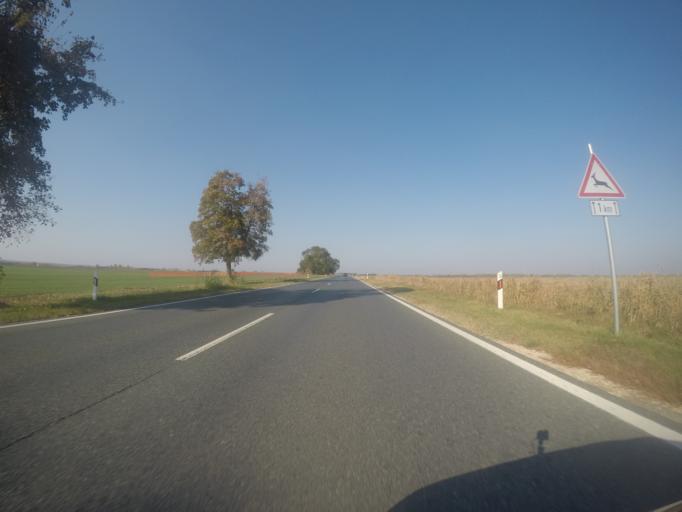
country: HU
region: Tolna
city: Madocsa
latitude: 46.7180
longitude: 18.8860
